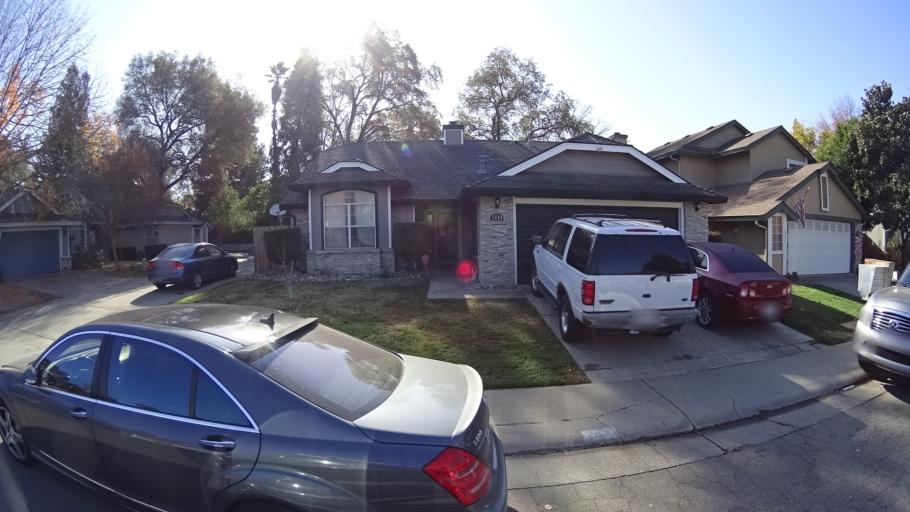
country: US
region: California
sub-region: Sacramento County
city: Citrus Heights
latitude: 38.6888
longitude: -121.2867
